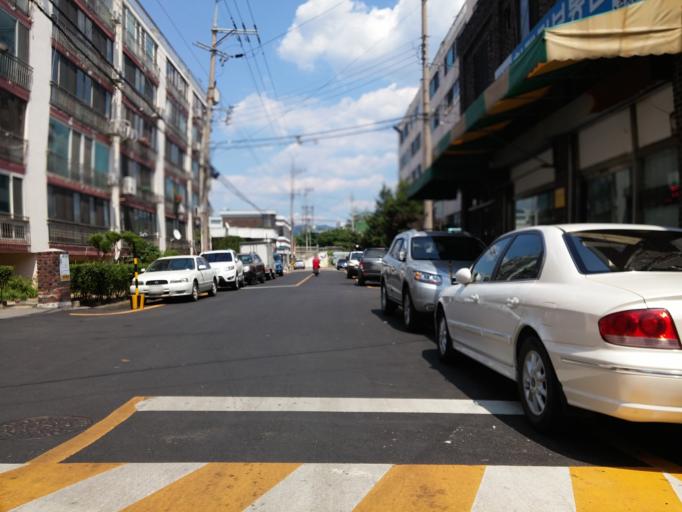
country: KR
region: Chungcheongbuk-do
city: Cheongju-si
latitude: 36.6180
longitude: 127.4908
